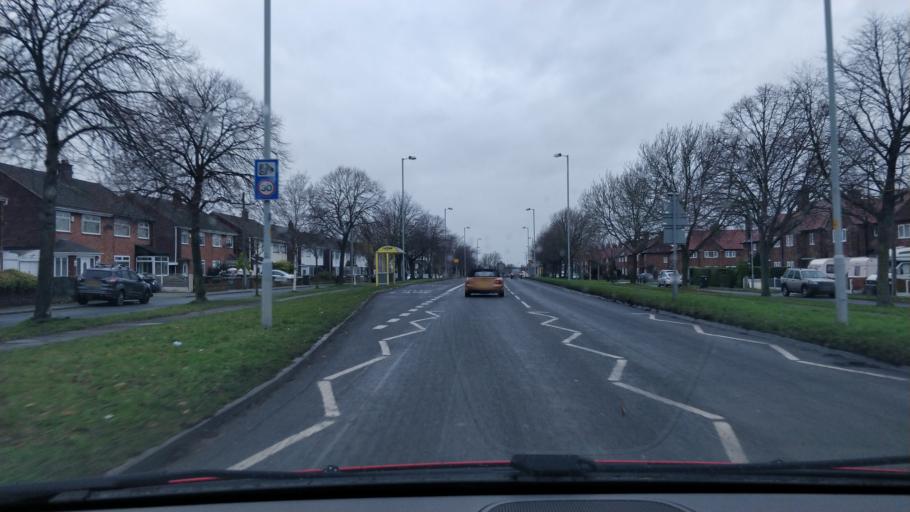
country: GB
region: England
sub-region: Sefton
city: Litherland
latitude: 53.4777
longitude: -2.9958
